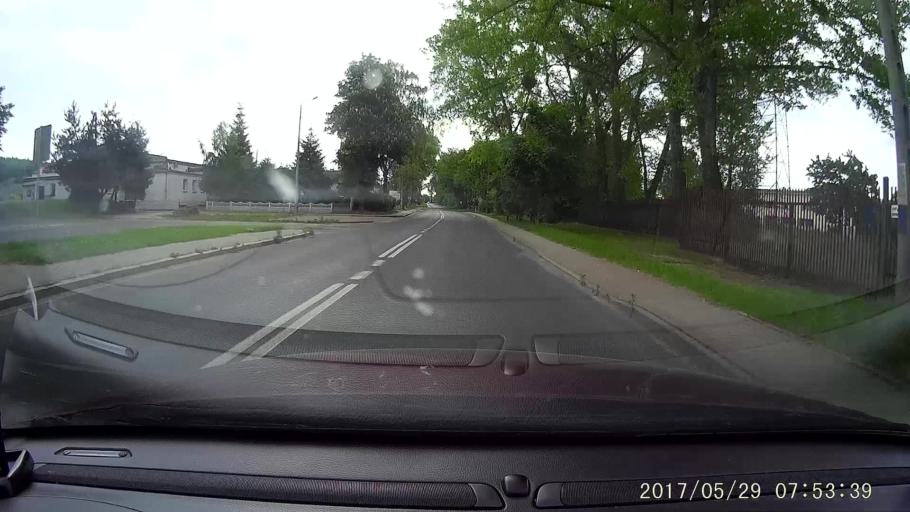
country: PL
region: Lower Silesian Voivodeship
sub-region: Powiat zlotoryjski
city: Olszanica
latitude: 51.2167
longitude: 15.7343
